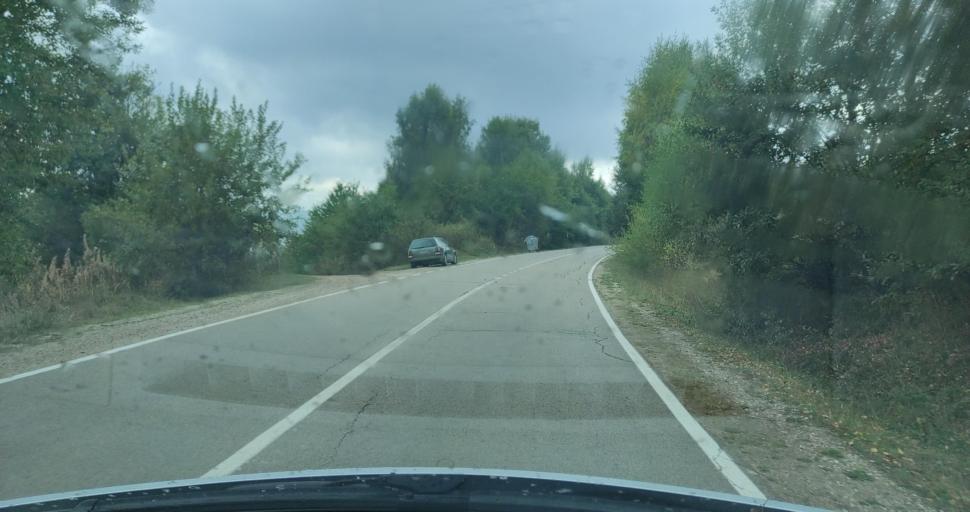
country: RS
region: Central Serbia
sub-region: Jablanicki Okrug
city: Crna Trava
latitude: 42.7079
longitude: 22.3284
